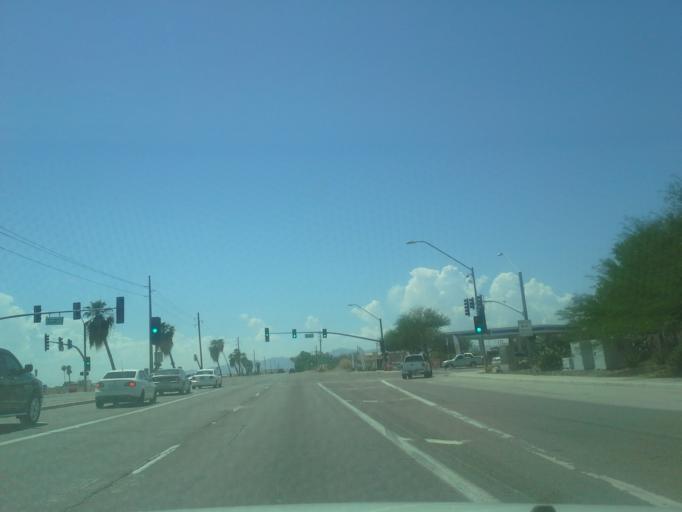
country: US
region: Arizona
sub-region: Maricopa County
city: Peoria
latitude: 33.5372
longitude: -112.2715
